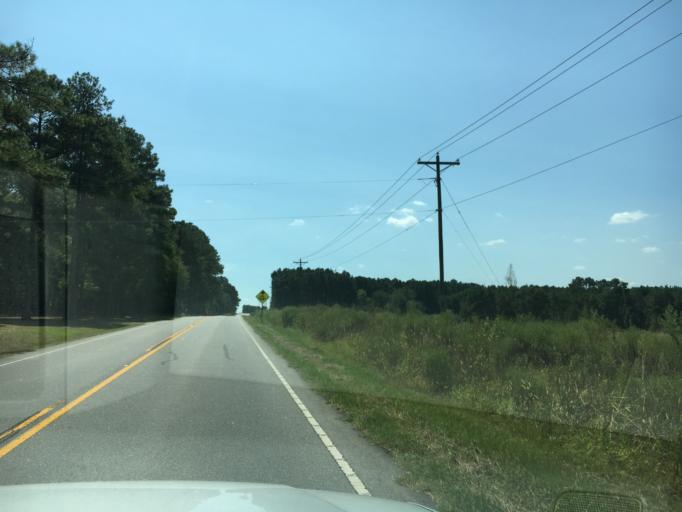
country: US
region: South Carolina
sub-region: Saluda County
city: Saluda
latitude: 33.9078
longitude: -81.7027
